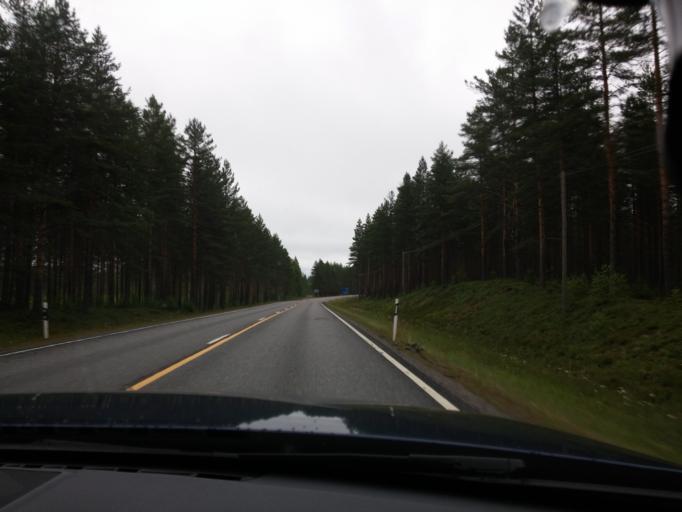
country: FI
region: Pirkanmaa
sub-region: Ylae-Pirkanmaa
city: Vilppula
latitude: 61.9443
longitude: 24.5419
